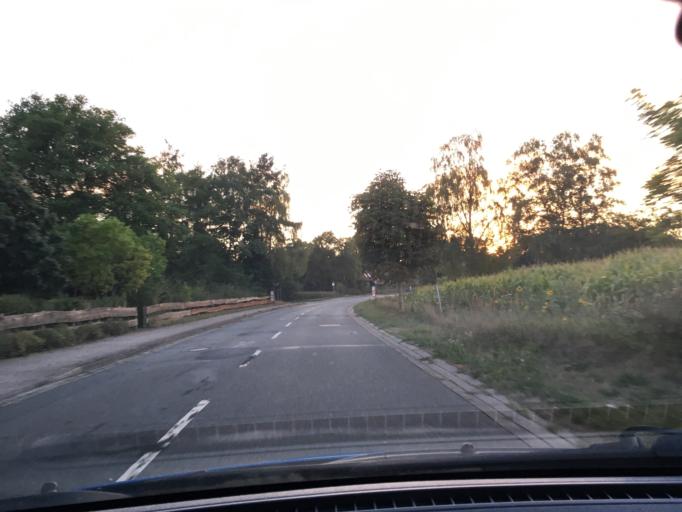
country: DE
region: Lower Saxony
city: Fassberg
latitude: 52.8962
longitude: 10.1375
